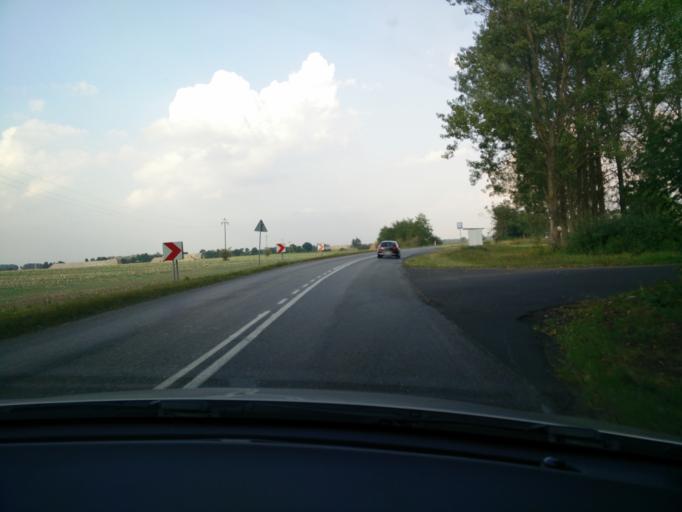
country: PL
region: Greater Poland Voivodeship
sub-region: Powiat sredzki
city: Dominowo
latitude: 52.2637
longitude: 17.4282
